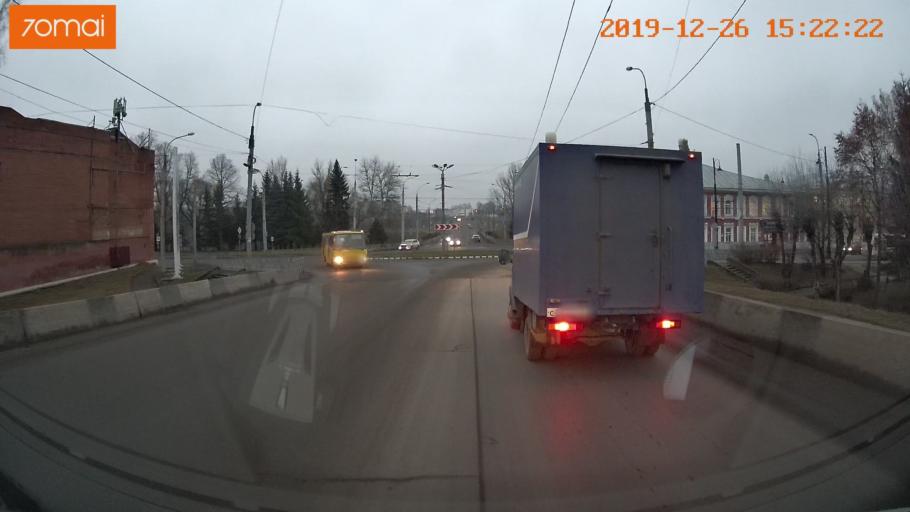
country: RU
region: Jaroslavl
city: Rybinsk
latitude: 58.0482
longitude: 38.8601
